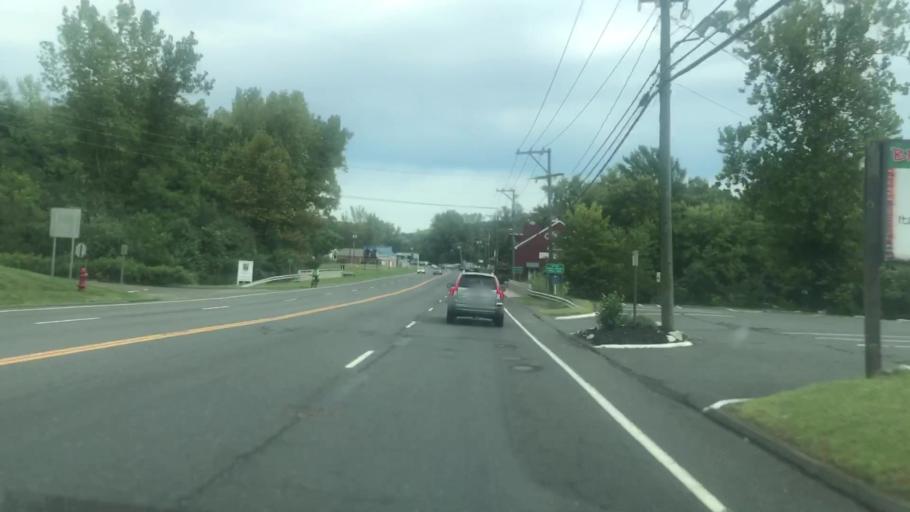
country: US
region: Connecticut
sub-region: Litchfield County
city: New Milford
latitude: 41.5684
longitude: -73.4143
